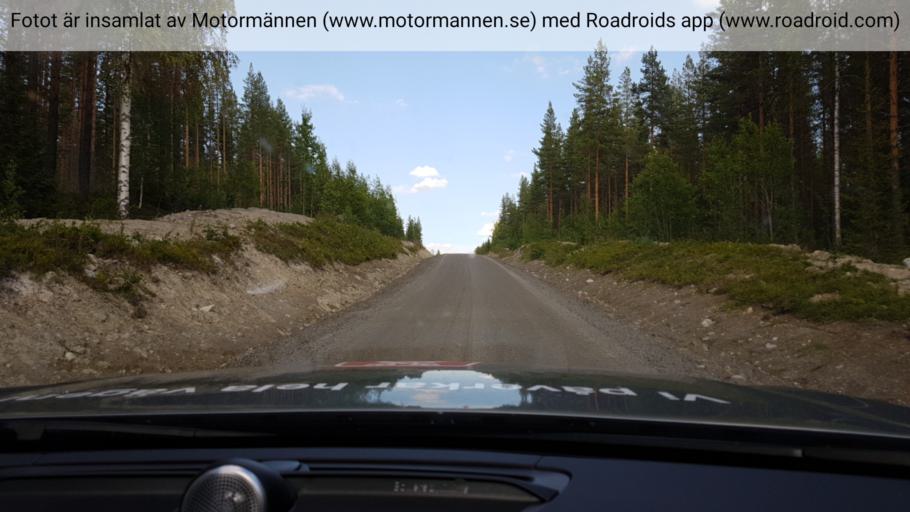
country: SE
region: Vaesterbotten
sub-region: Dorotea Kommun
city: Dorotea
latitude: 63.9303
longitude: 16.1470
